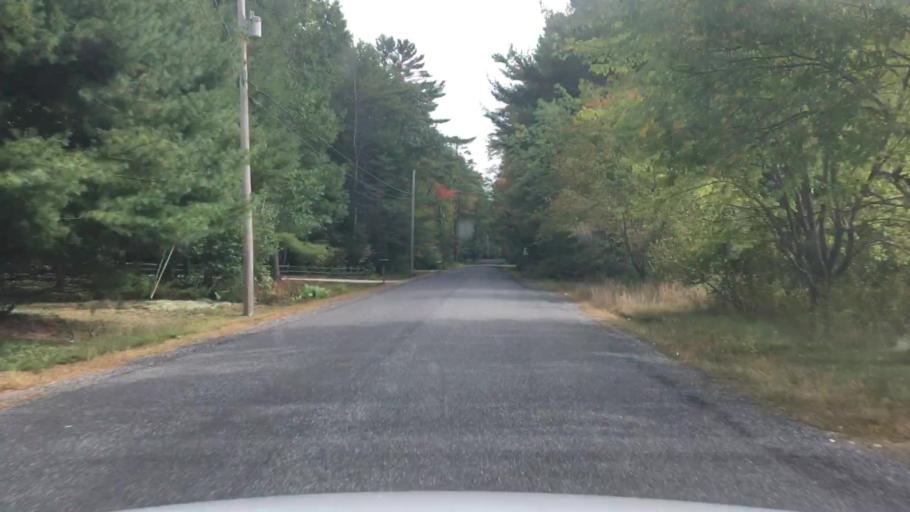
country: US
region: Maine
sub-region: Androscoggin County
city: Lisbon Falls
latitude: 43.9821
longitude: -70.0984
